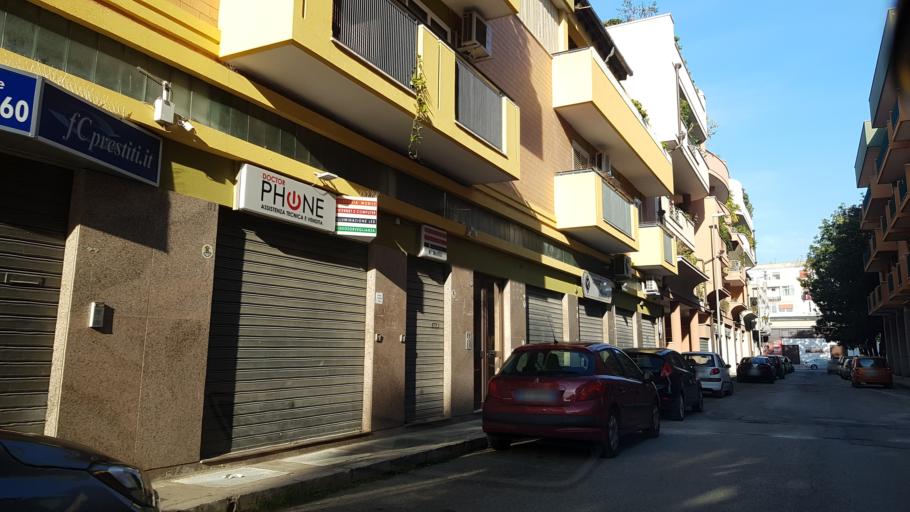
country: IT
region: Apulia
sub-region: Provincia di Brindisi
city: Brindisi
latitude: 40.6337
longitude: 17.9353
